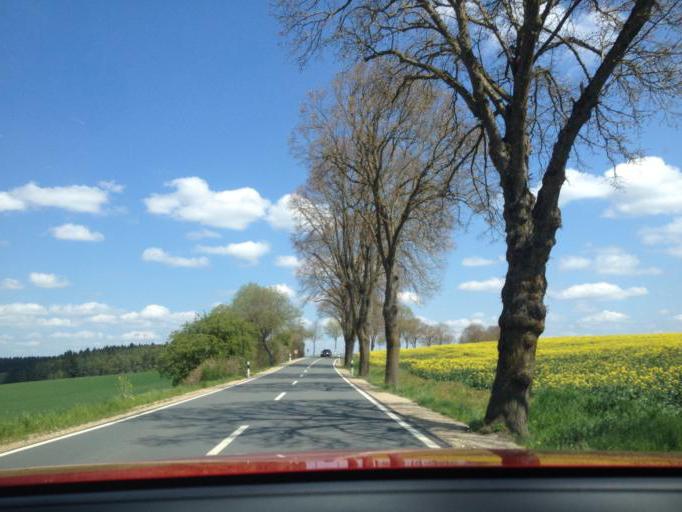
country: DE
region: Bavaria
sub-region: Upper Franconia
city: Pottenstein
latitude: 49.7131
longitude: 11.4433
